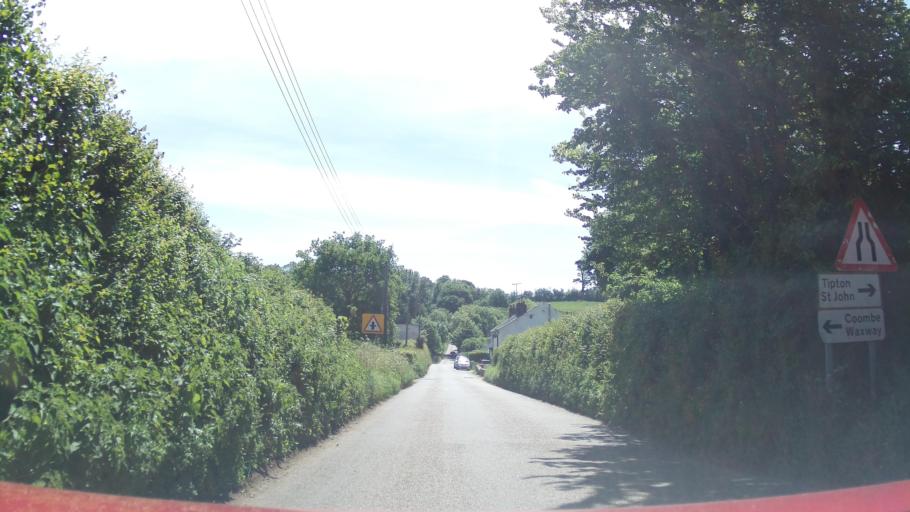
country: GB
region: England
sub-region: Devon
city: Newton Poppleford
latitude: 50.7212
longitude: -3.2836
